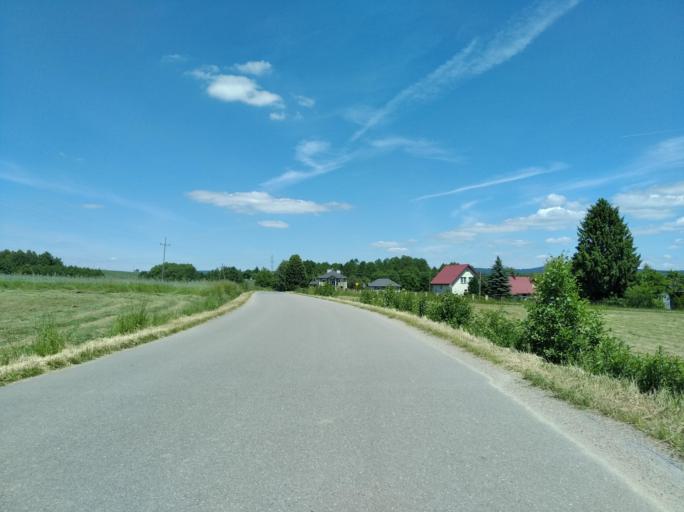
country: PL
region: Subcarpathian Voivodeship
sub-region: Powiat krosnienski
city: Wojaszowka
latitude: 49.7716
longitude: 21.6454
